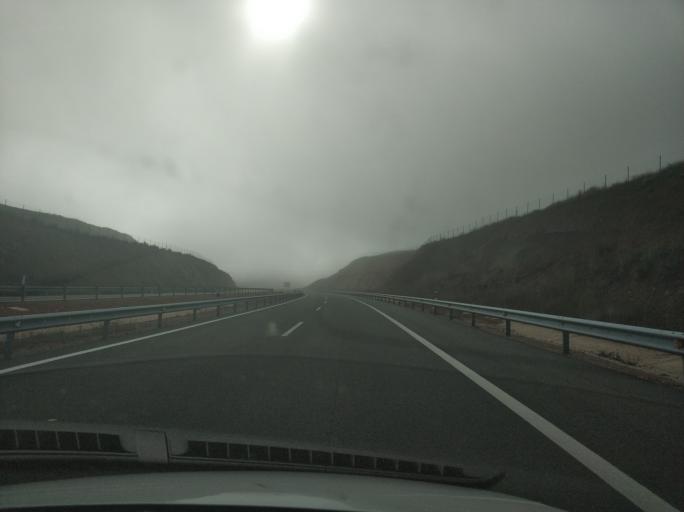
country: ES
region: Castille and Leon
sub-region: Provincia de Soria
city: Yelo
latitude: 41.2344
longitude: -2.4793
